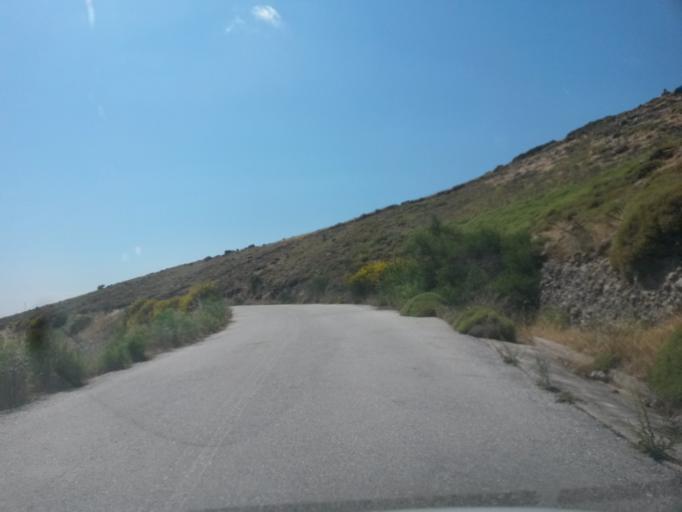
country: GR
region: North Aegean
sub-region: Nomos Lesvou
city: Eresos
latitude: 39.2102
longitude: 25.9006
